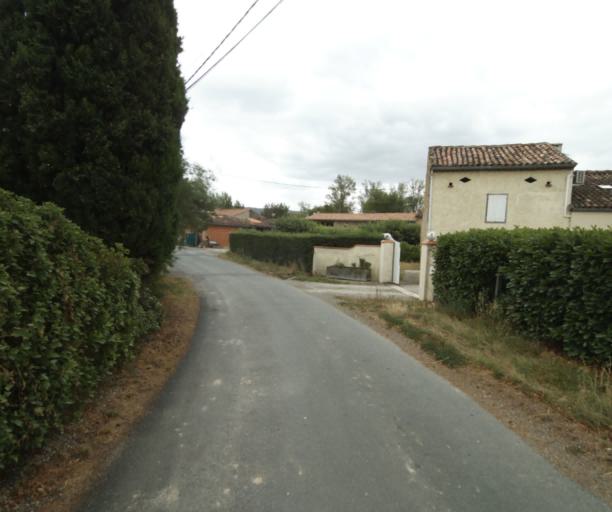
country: FR
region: Midi-Pyrenees
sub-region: Departement du Tarn
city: Soreze
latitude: 43.4671
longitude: 2.0557
